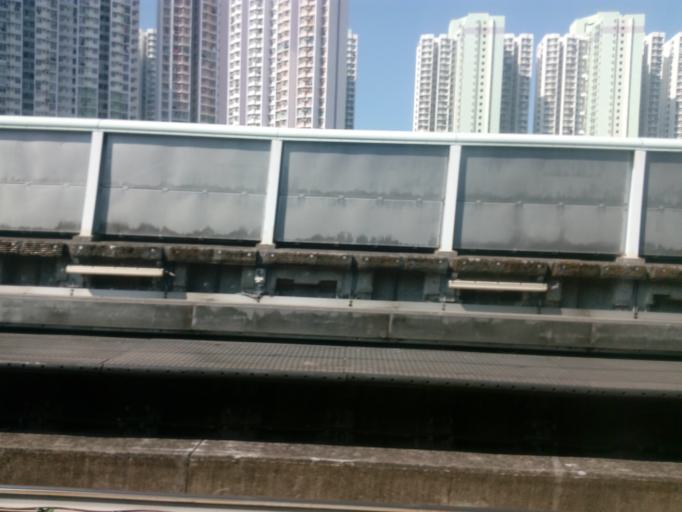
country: HK
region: Sai Kung
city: Sai Kung
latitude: 22.4224
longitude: 114.2275
